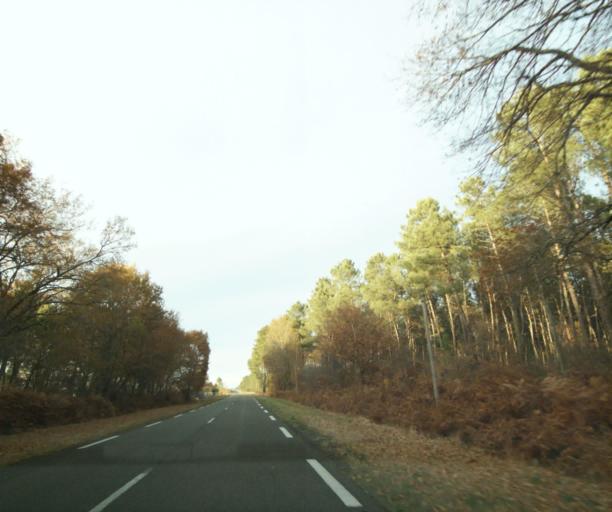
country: FR
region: Aquitaine
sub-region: Departement de la Gironde
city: Grignols
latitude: 44.1950
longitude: -0.1552
